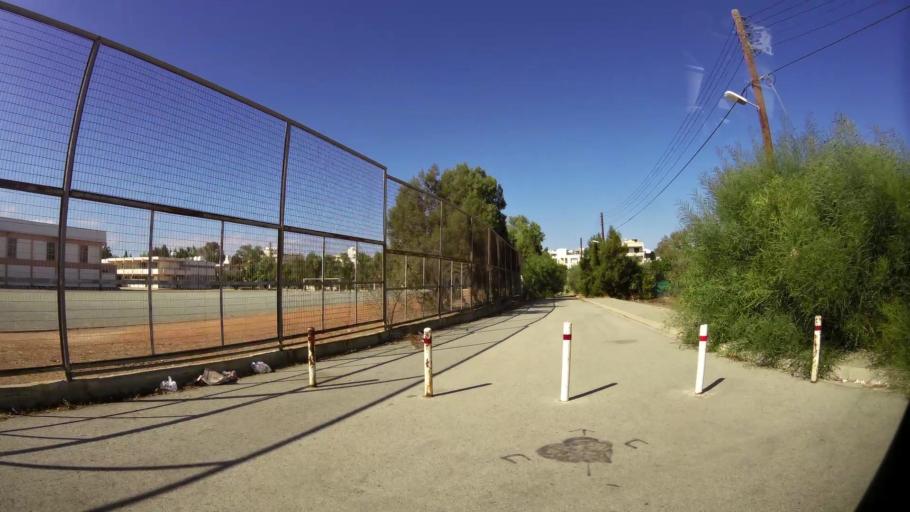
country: CY
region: Lefkosia
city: Nicosia
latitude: 35.1377
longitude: 33.3380
